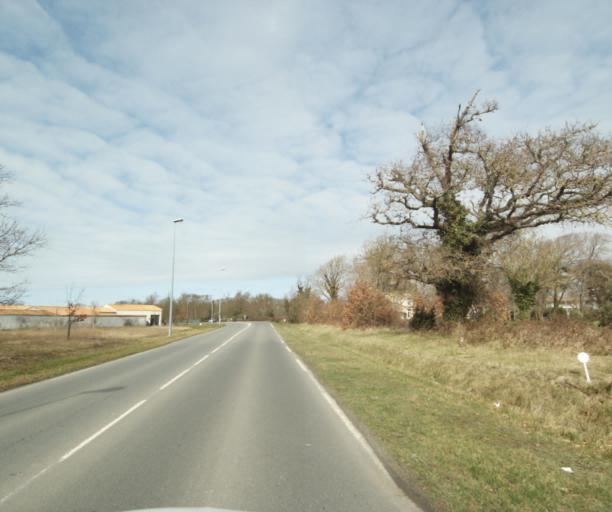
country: FR
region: Poitou-Charentes
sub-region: Departement de la Charente-Maritime
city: Lagord
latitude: 46.1834
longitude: -1.1740
